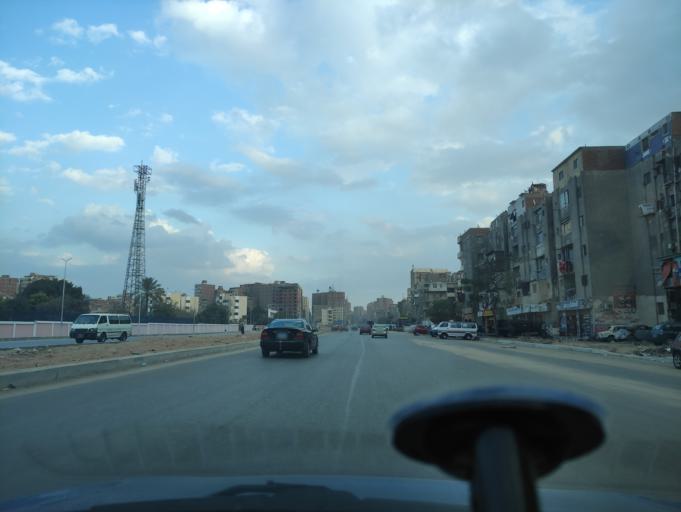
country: EG
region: Muhafazat al Qalyubiyah
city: Al Khankah
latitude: 30.1357
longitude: 31.3530
